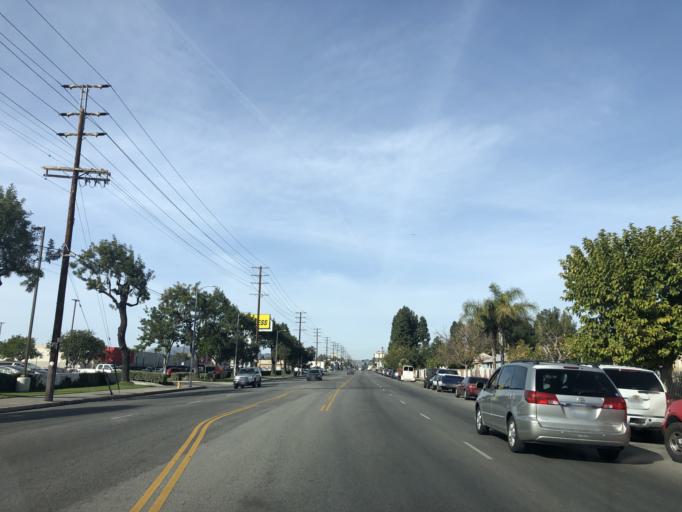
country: US
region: California
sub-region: Los Angeles County
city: San Fernando
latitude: 34.2442
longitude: -118.4167
